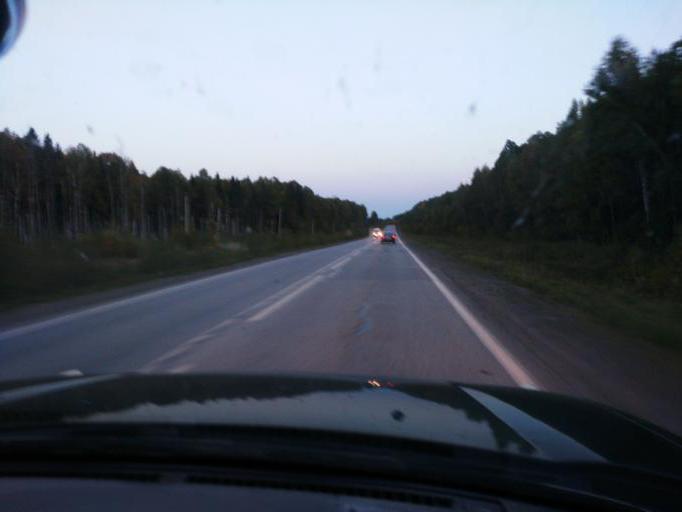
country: RU
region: Perm
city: Verkhnechusovskiye Gorodki
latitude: 58.2692
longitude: 56.9533
